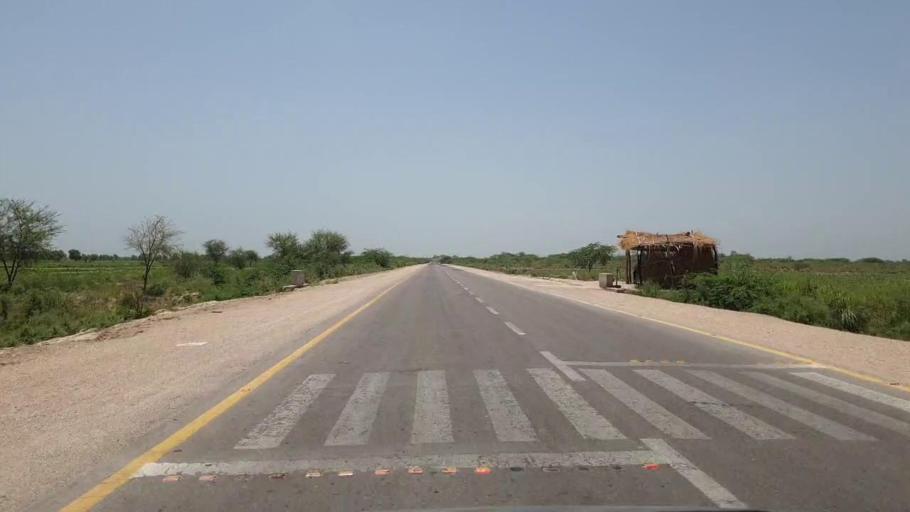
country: PK
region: Sindh
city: Sakrand
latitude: 26.1193
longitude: 68.3848
